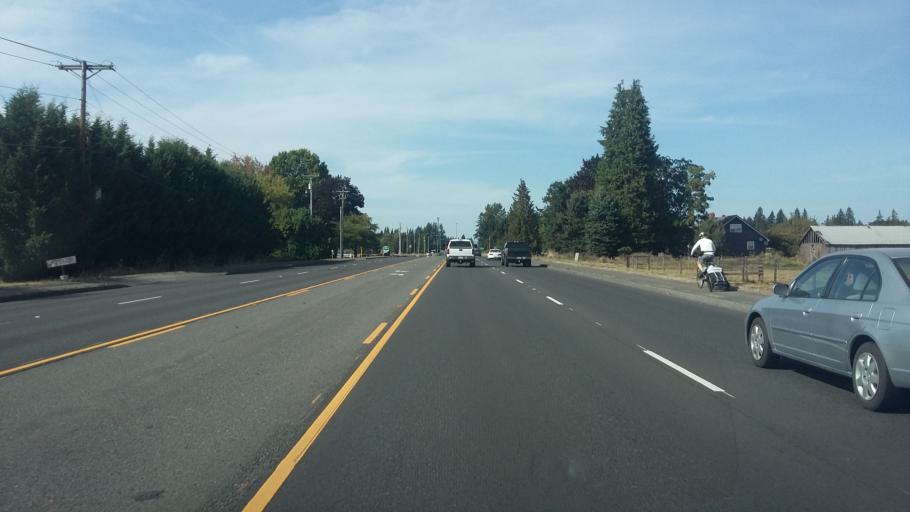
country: US
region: Washington
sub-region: Clark County
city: Brush Prairie
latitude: 45.7217
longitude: -122.5525
